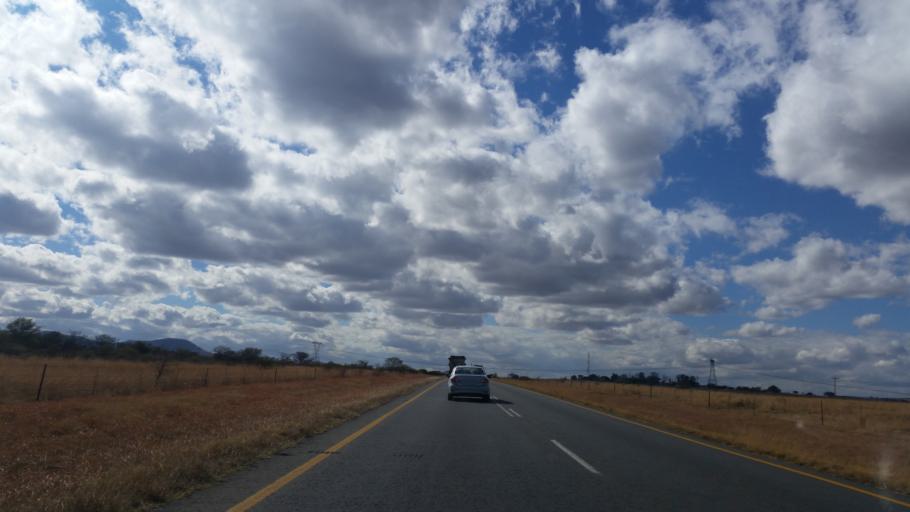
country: ZA
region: KwaZulu-Natal
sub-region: uThukela District Municipality
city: Ladysmith
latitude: -28.4805
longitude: 29.8518
